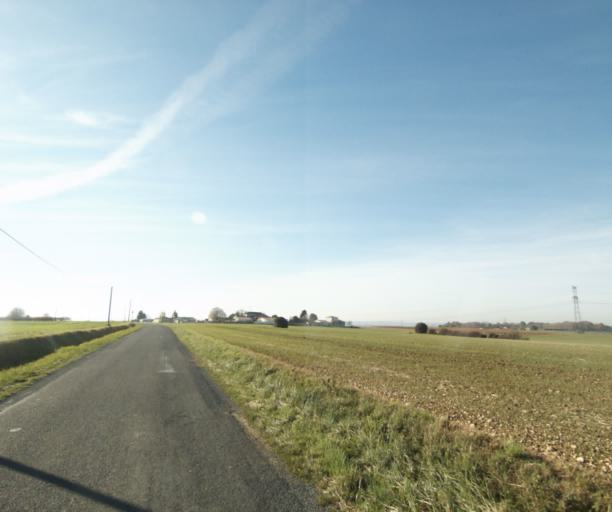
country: FR
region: Poitou-Charentes
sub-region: Departement de la Charente-Maritime
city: Chaniers
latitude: 45.7389
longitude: -0.5747
